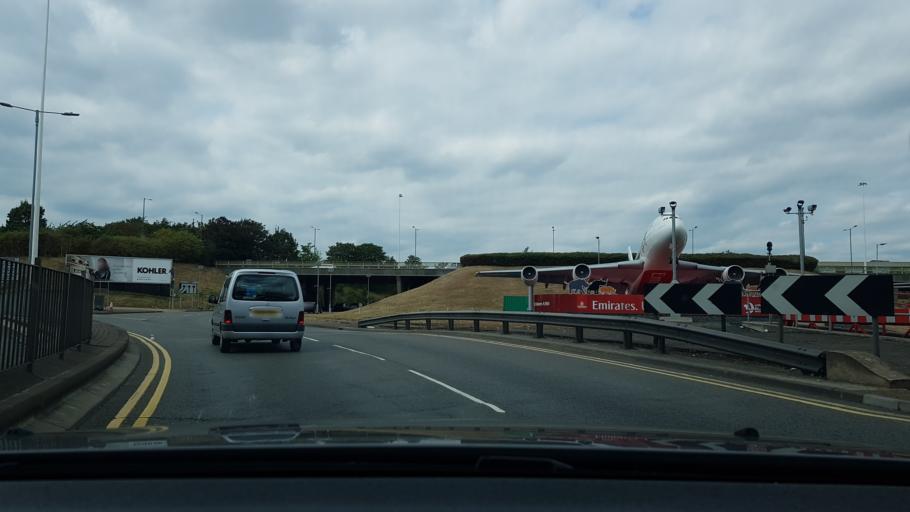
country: GB
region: England
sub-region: Greater London
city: West Drayton
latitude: 51.4759
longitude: -0.4529
